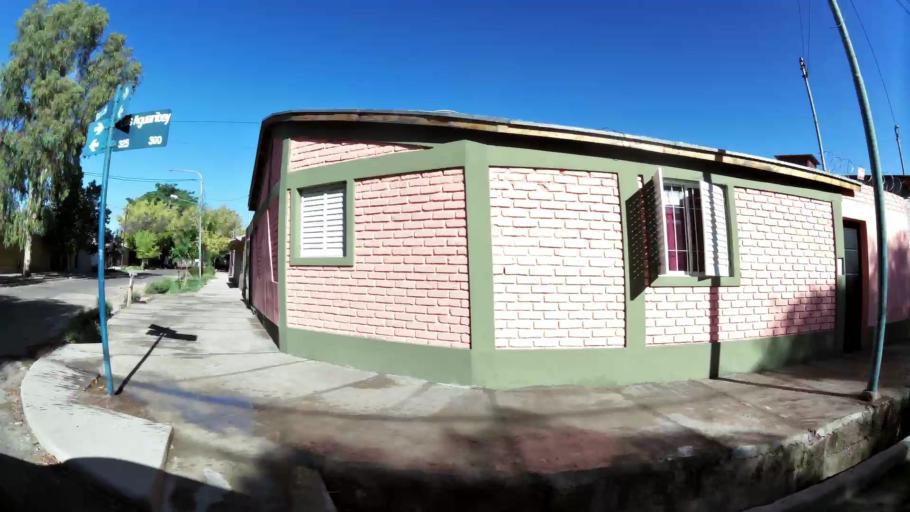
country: AR
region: Mendoza
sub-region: Departamento de Godoy Cruz
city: Godoy Cruz
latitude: -32.9281
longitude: -68.8642
